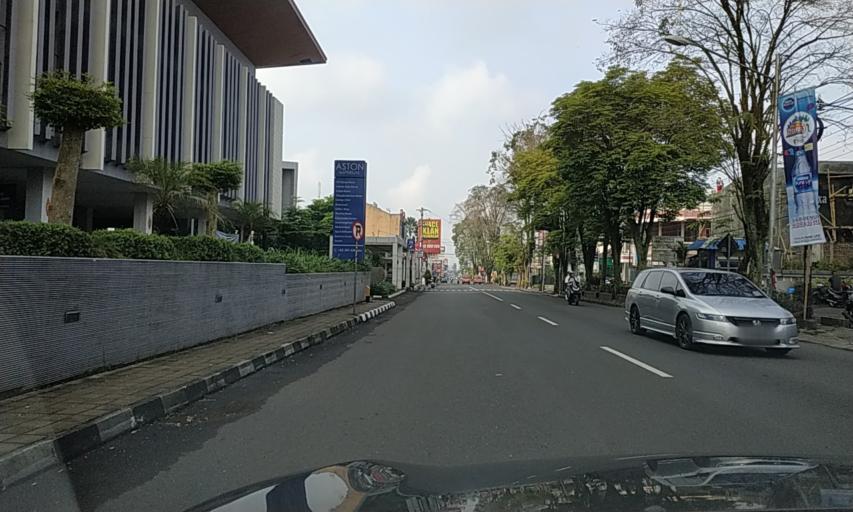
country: ID
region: Central Java
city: Purwokerto
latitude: -7.4175
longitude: 109.2447
